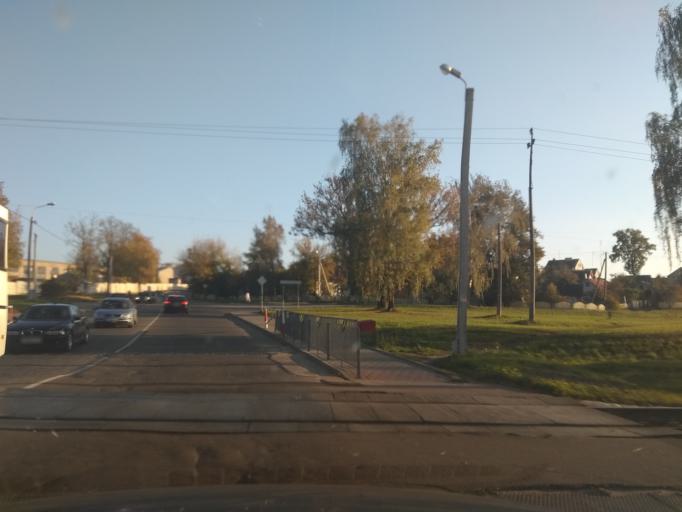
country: BY
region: Grodnenskaya
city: Vawkavysk
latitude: 53.1563
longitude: 24.4557
